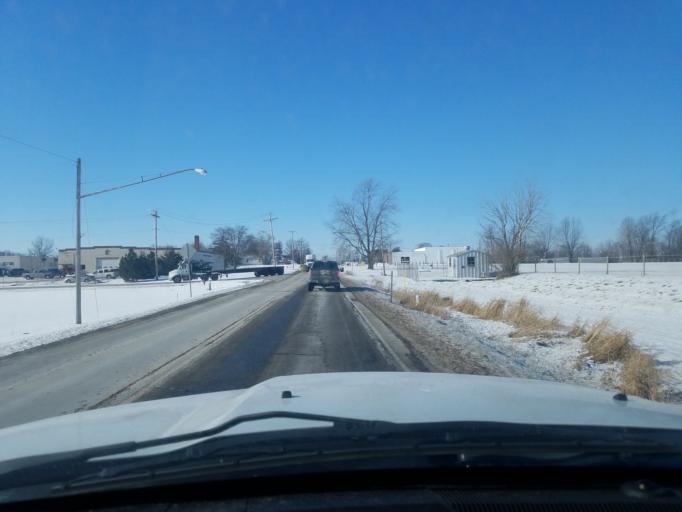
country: US
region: Indiana
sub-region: Noble County
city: Albion
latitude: 41.3959
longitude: -85.4092
